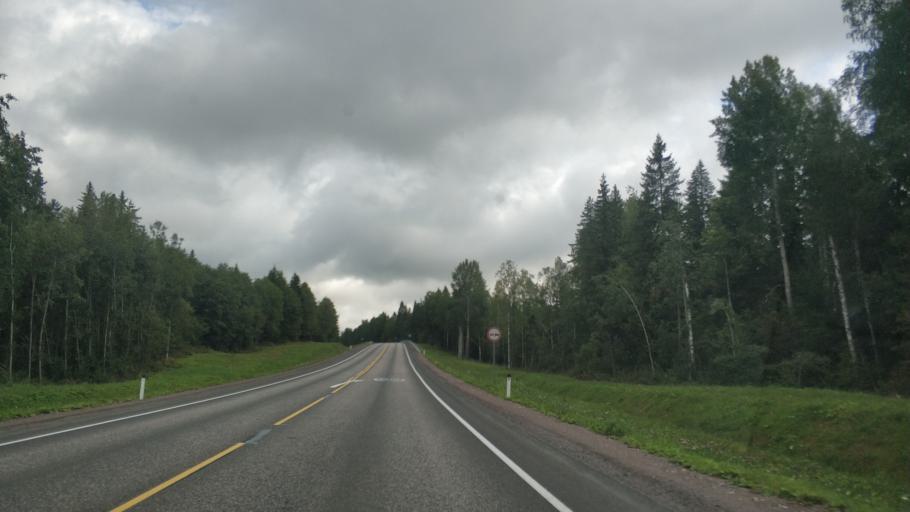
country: RU
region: Republic of Karelia
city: Khelyulya
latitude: 61.8369
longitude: 30.6425
